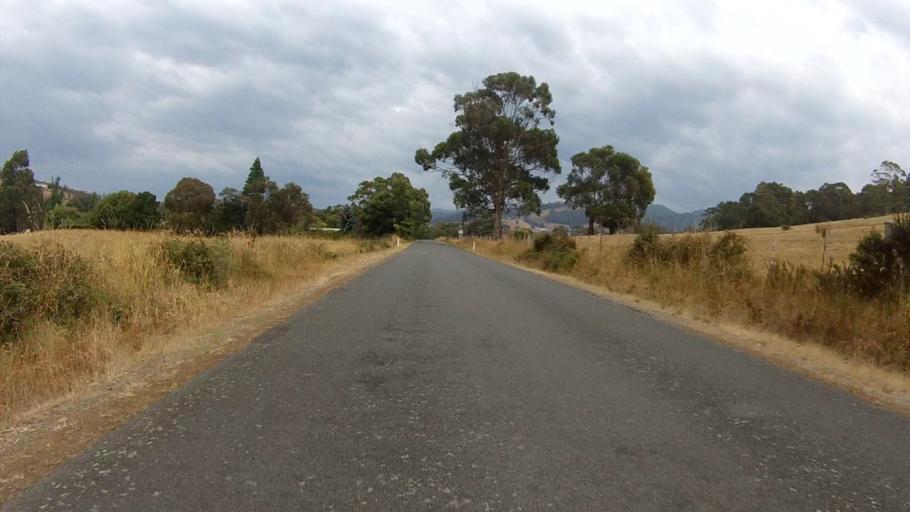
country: AU
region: Tasmania
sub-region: Huon Valley
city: Cygnet
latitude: -43.1832
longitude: 147.1106
